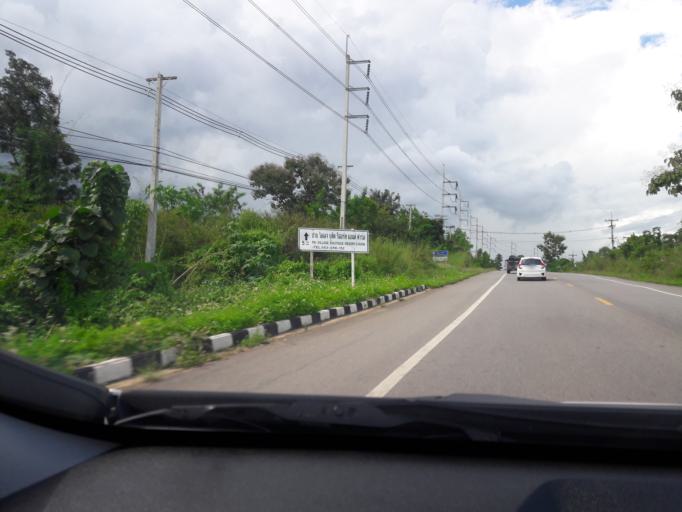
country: TH
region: Mae Hong Son
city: Mae Hi
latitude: 19.3322
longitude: 98.4332
